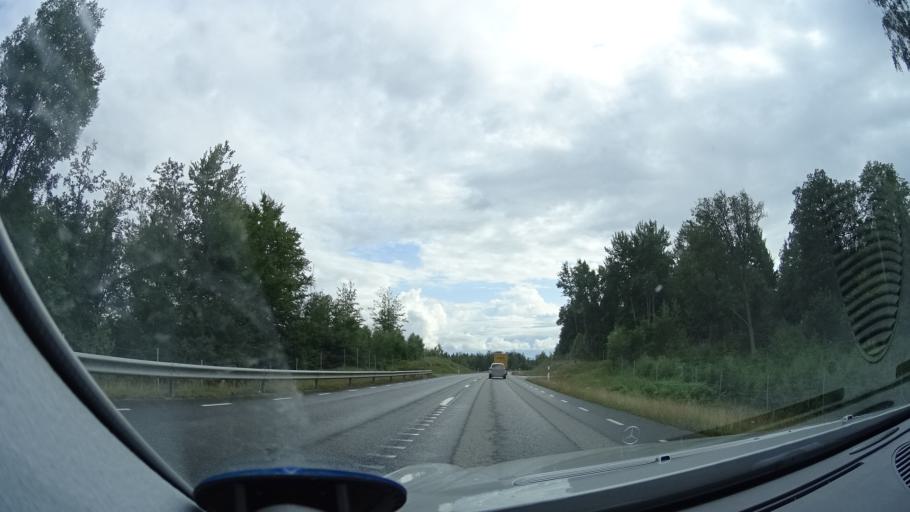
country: SE
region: Blekinge
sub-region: Karlshamns Kommun
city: Svangsta
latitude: 56.2996
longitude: 14.8823
